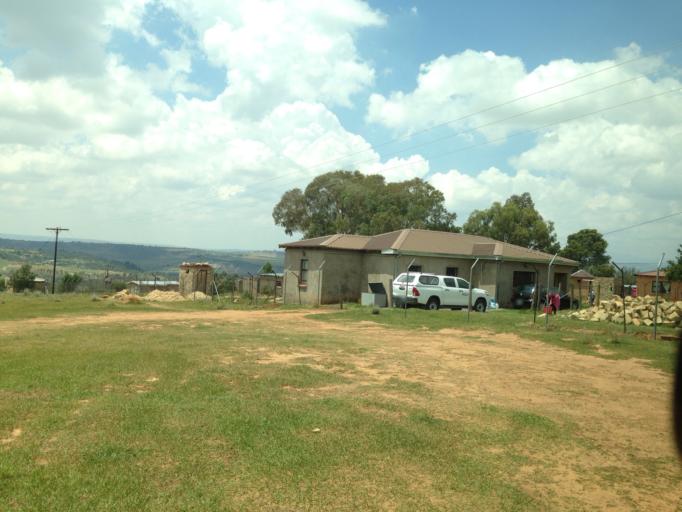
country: LS
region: Maseru
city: Maseru
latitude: -29.4494
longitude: 27.5645
